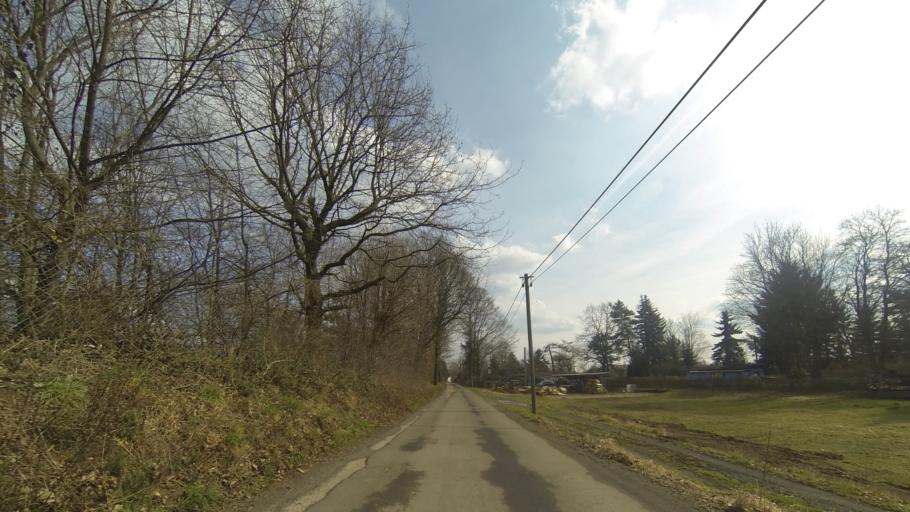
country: DE
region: Saxony
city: Radeburg
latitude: 51.2238
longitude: 13.7179
